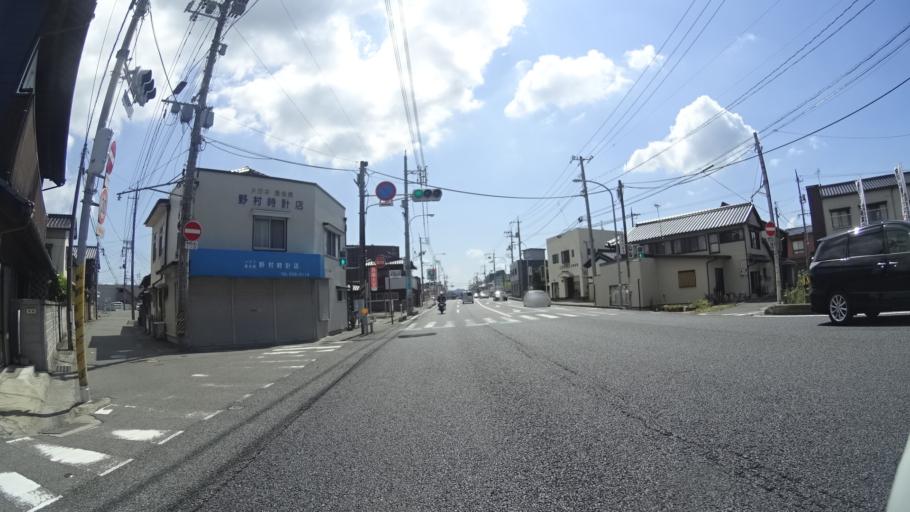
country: JP
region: Yamaguchi
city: Shimonoseki
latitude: 34.0267
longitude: 130.9138
